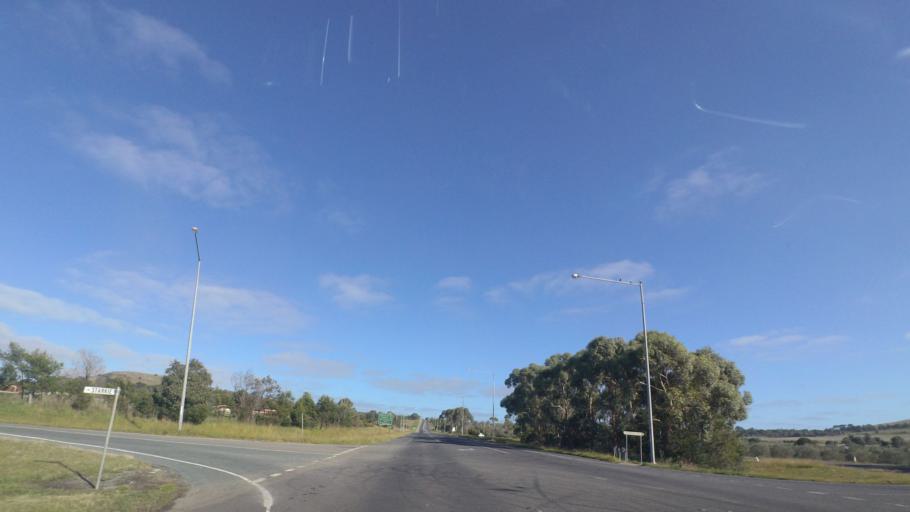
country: AU
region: Victoria
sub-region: Hume
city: Sunbury
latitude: -37.5386
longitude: 144.6517
